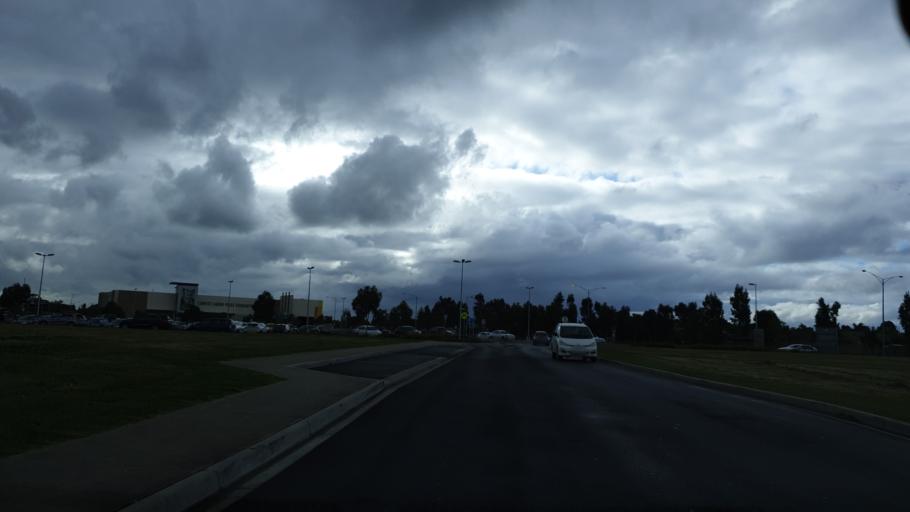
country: AU
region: Victoria
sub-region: Casey
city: Cranbourne
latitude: -38.0998
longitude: 145.2960
